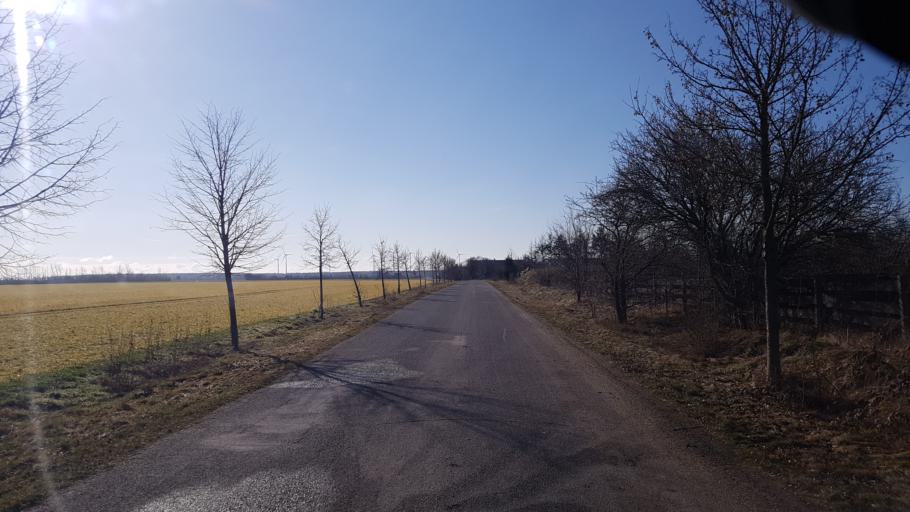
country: DE
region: Brandenburg
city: Muhlberg
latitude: 51.5059
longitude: 13.2308
